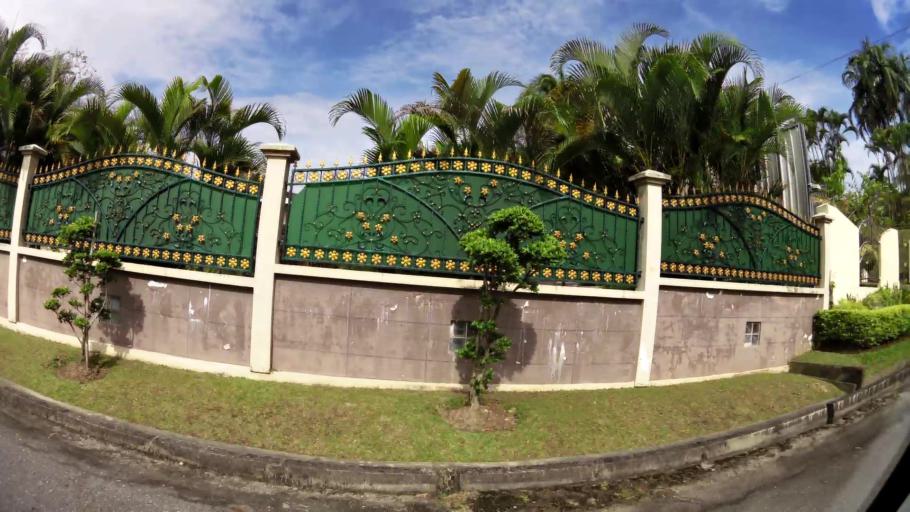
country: BN
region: Brunei and Muara
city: Bandar Seri Begawan
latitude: 4.8905
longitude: 114.8958
